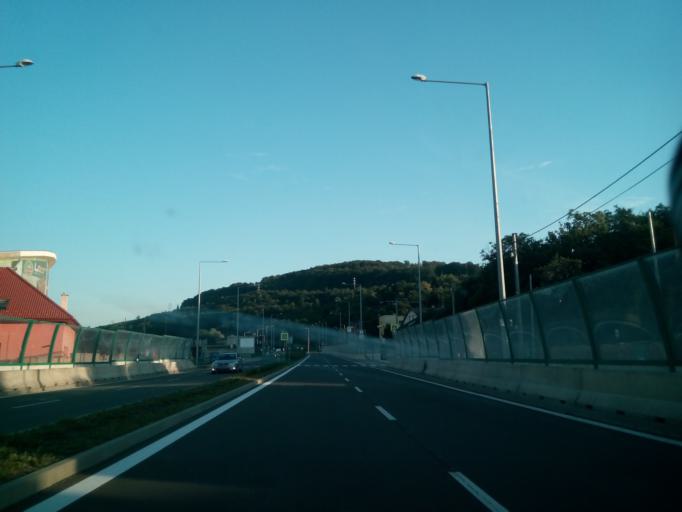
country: SK
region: Presovsky
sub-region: Okres Presov
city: Presov
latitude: 48.9887
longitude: 21.2292
